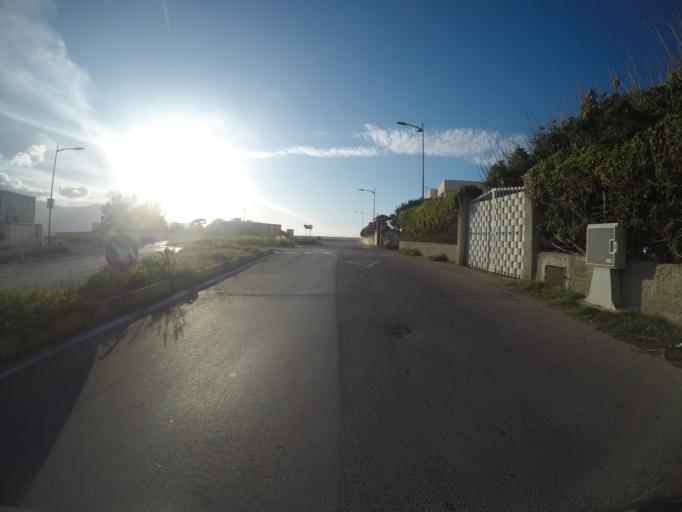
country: IT
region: Sicily
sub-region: Palermo
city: Isola delle Femmine
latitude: 38.1994
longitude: 13.2442
